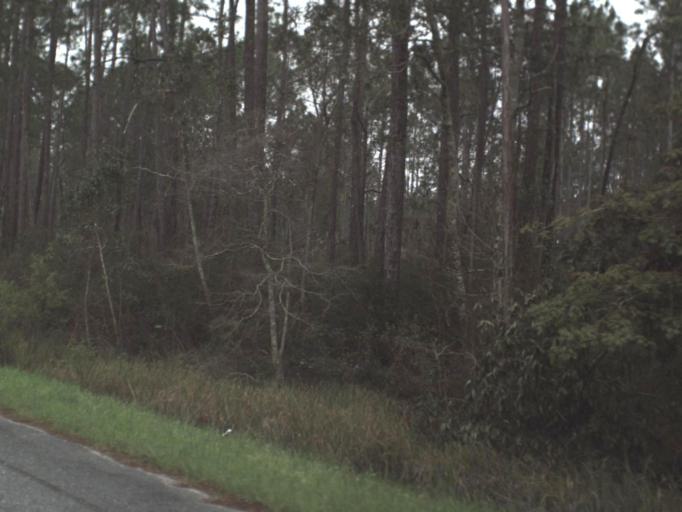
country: US
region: Florida
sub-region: Franklin County
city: Eastpoint
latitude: 29.8231
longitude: -84.9109
